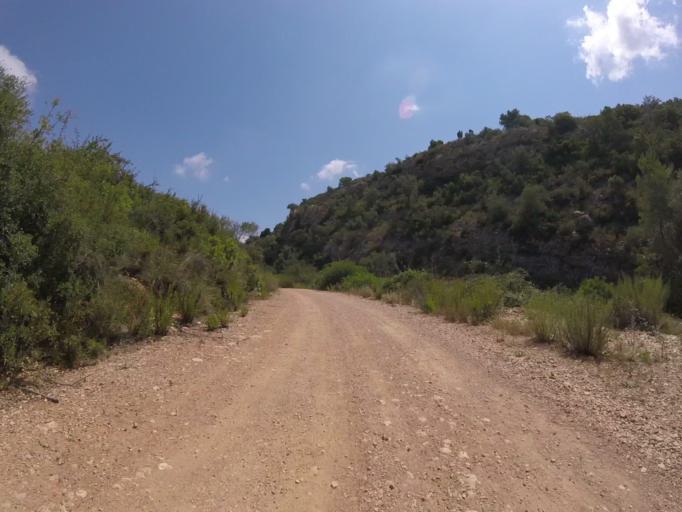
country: ES
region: Valencia
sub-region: Provincia de Castello
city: Torreblanca
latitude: 40.2066
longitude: 0.1381
